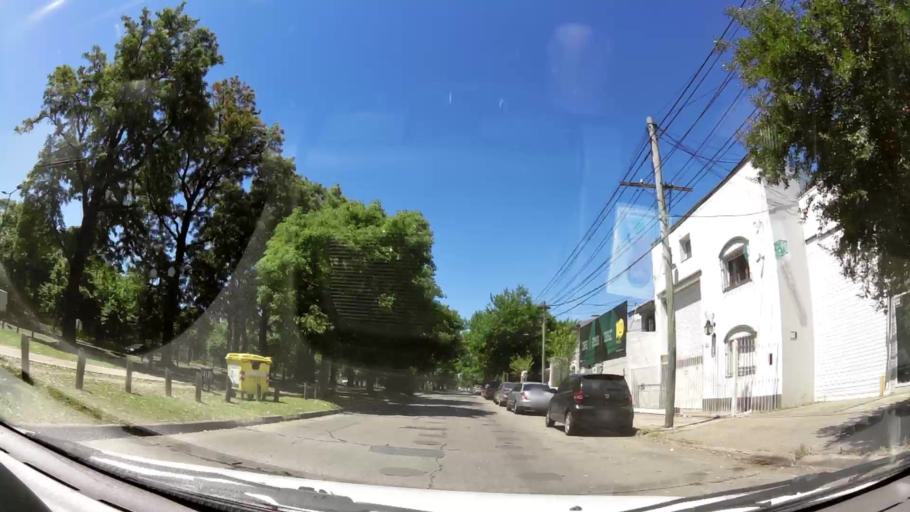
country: AR
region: Buenos Aires
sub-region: Partido de San Isidro
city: San Isidro
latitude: -34.4873
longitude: -58.5198
